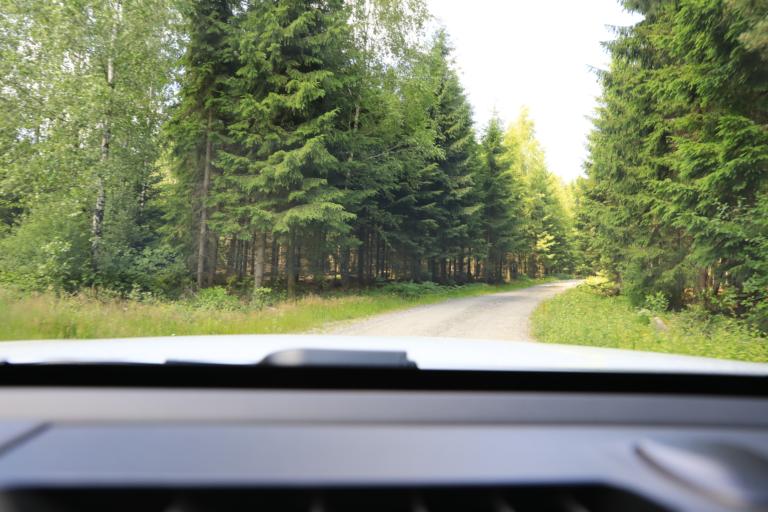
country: SE
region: Halland
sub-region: Varbergs Kommun
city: Tvaaker
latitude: 57.0965
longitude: 12.4841
